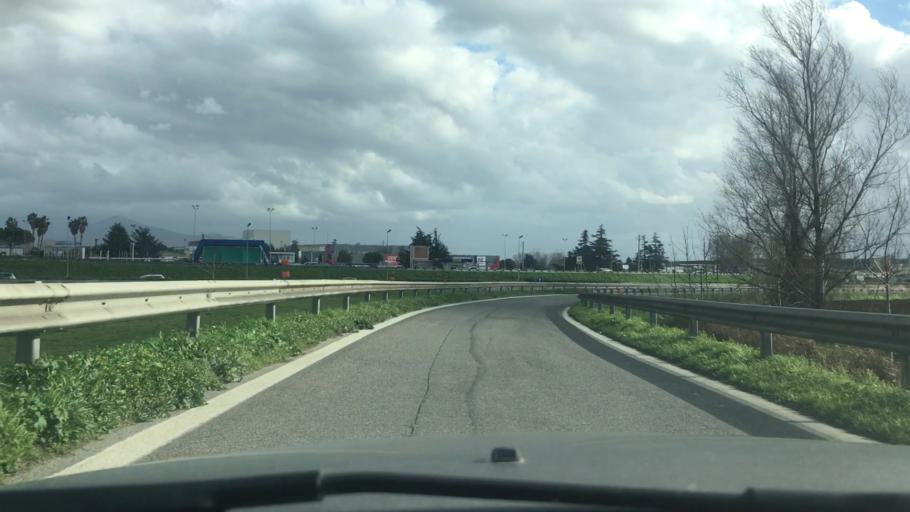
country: IT
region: Campania
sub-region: Provincia di Caserta
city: Marcianise
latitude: 41.0182
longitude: 14.3211
